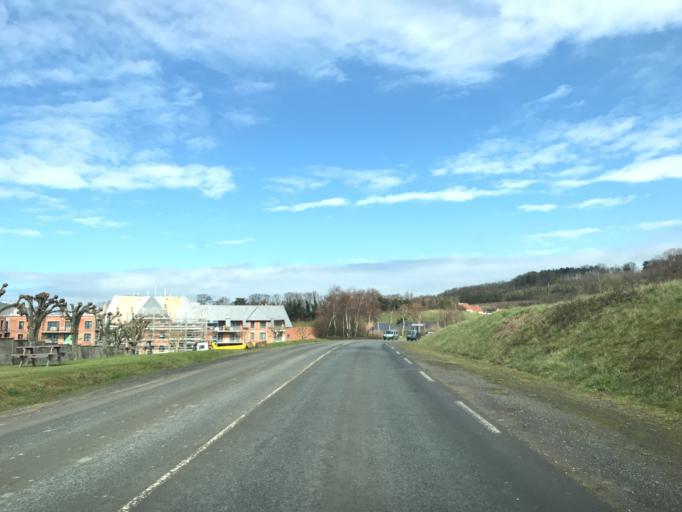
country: FR
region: Lower Normandy
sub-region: Departement du Calvados
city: Dives-sur-Mer
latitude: 49.2844
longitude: -0.0939
